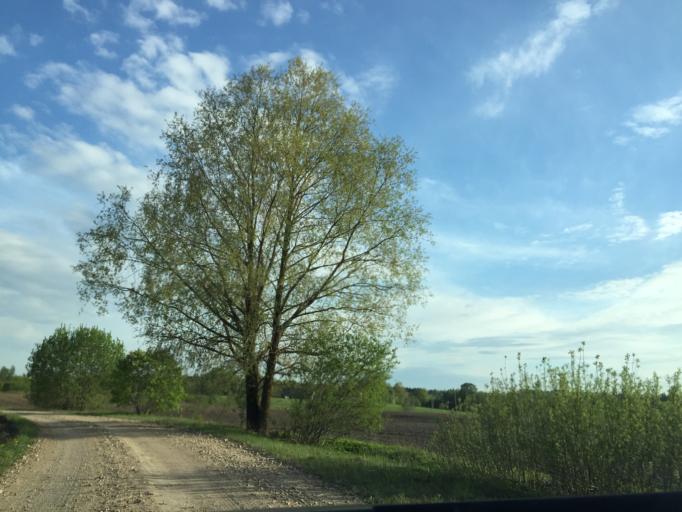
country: LV
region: Limbazu Rajons
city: Limbazi
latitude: 57.3776
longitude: 24.6375
